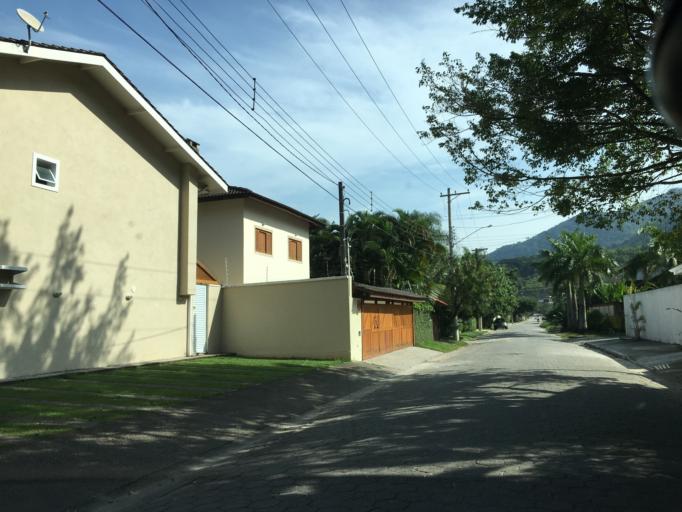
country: BR
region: Sao Paulo
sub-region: Sao Sebastiao
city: Sao Sebastiao
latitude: -23.7616
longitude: -45.7265
